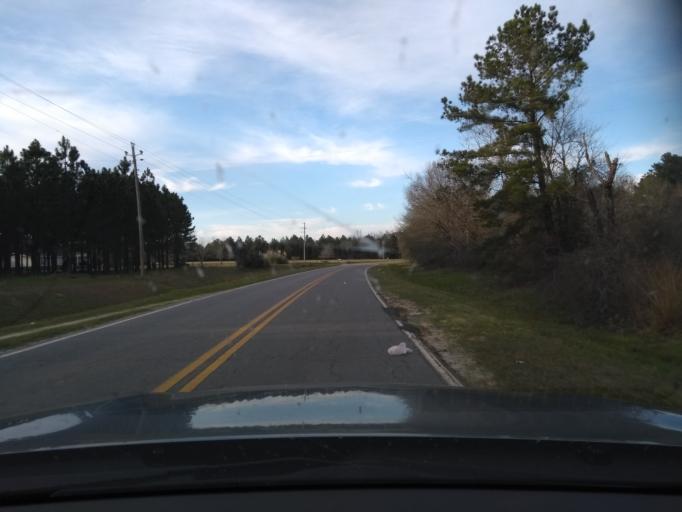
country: US
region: Georgia
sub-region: Evans County
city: Claxton
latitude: 32.2332
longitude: -81.7711
